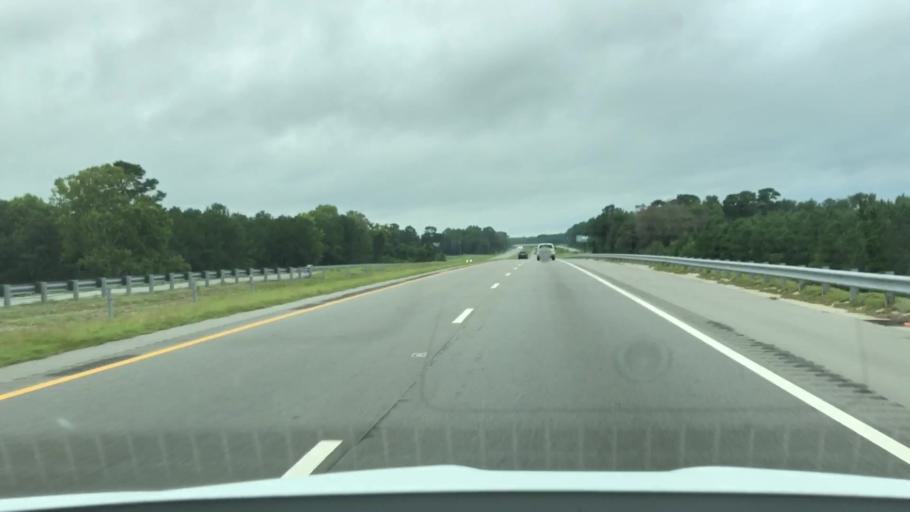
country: US
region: North Carolina
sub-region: Wayne County
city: Elroy
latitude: 35.3430
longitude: -77.8454
